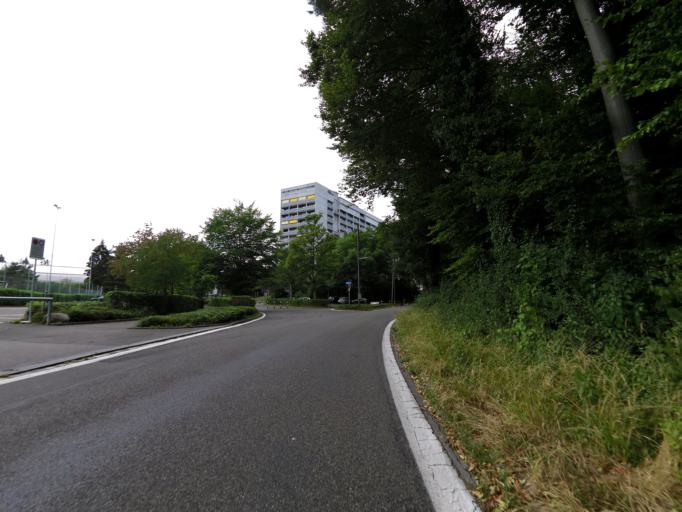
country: CH
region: Zurich
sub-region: Bezirk Zuerich
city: Zuerich (Kreis 11) / Affoltern
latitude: 47.4202
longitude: 8.5141
